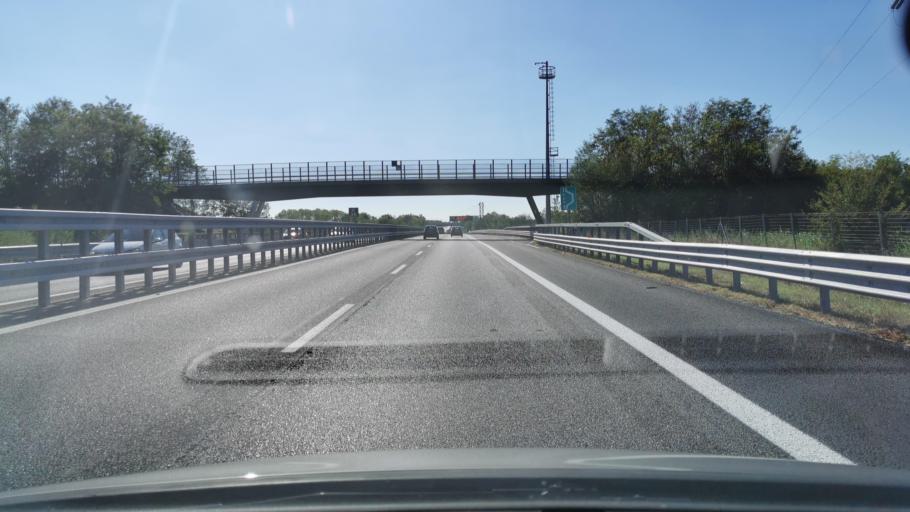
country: IT
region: Piedmont
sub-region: Provincia di Alessandria
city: Felizzano
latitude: 44.9146
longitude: 8.4300
